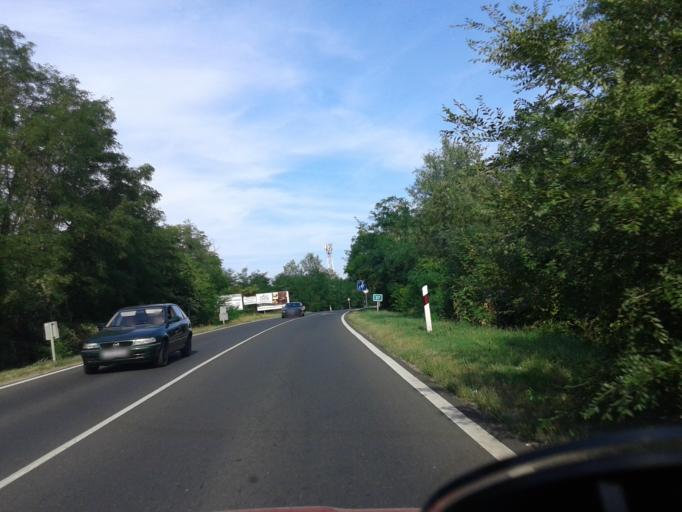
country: HU
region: Pest
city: Godollo
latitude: 47.5919
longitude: 19.3248
